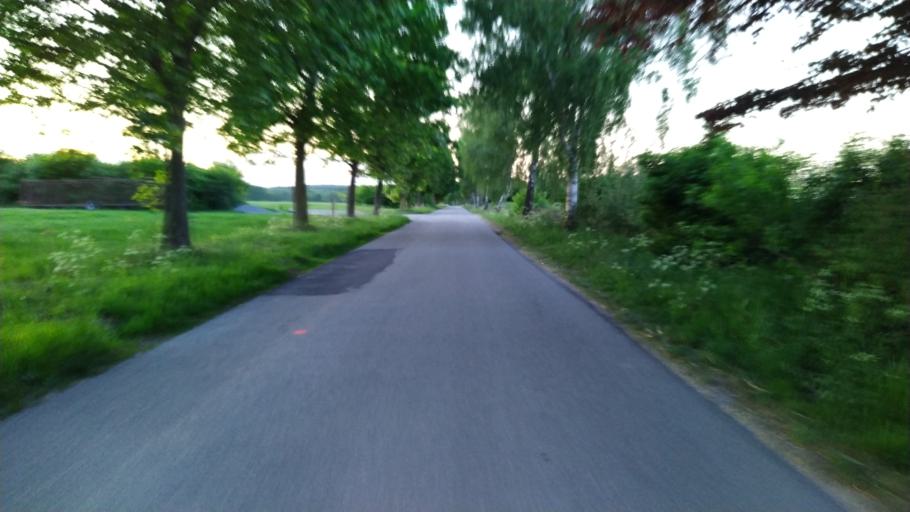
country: DE
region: Lower Saxony
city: Bargstedt
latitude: 53.4711
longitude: 9.4712
